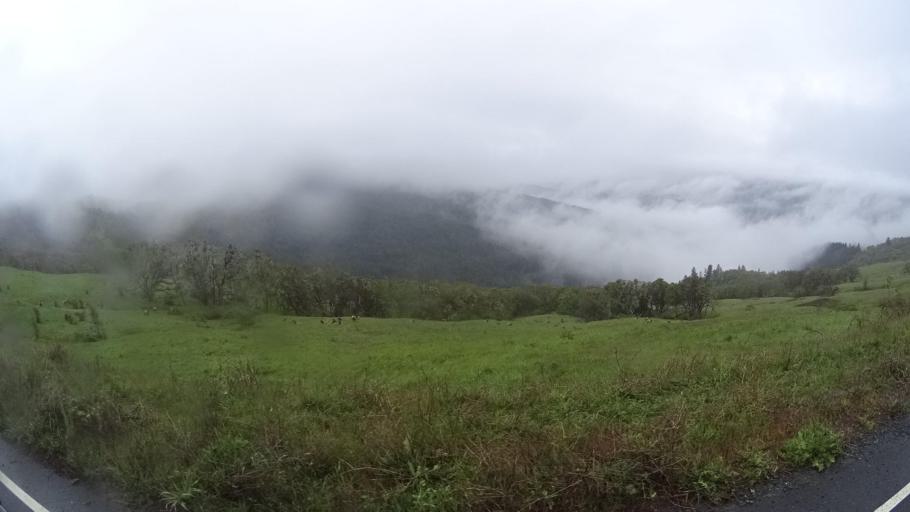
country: US
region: California
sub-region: Humboldt County
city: Westhaven-Moonstone
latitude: 41.1615
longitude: -123.8981
